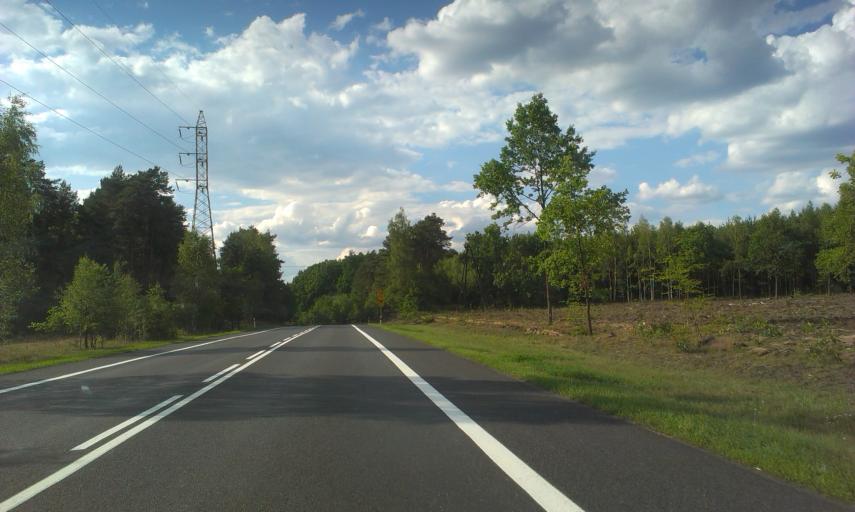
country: PL
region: Greater Poland Voivodeship
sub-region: Powiat pilski
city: Pila
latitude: 53.1788
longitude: 16.7742
